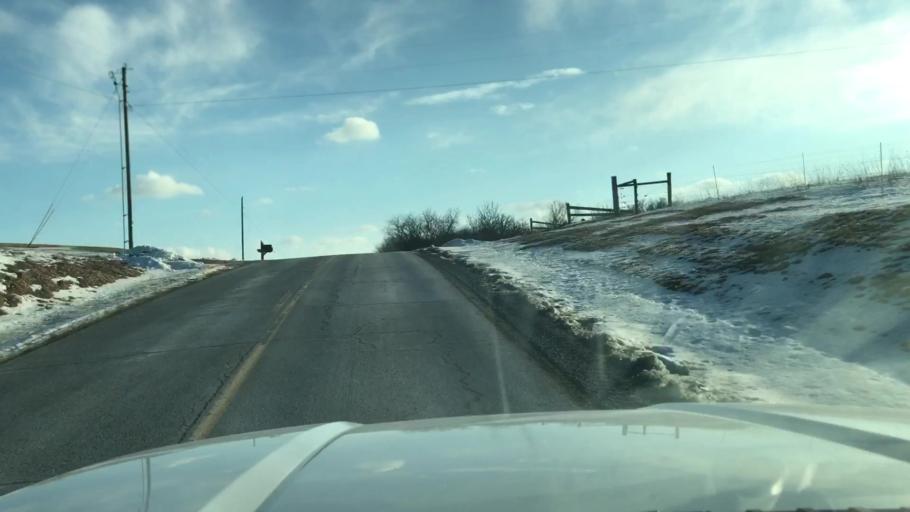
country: US
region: Missouri
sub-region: Holt County
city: Oregon
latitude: 40.0692
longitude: -94.9747
